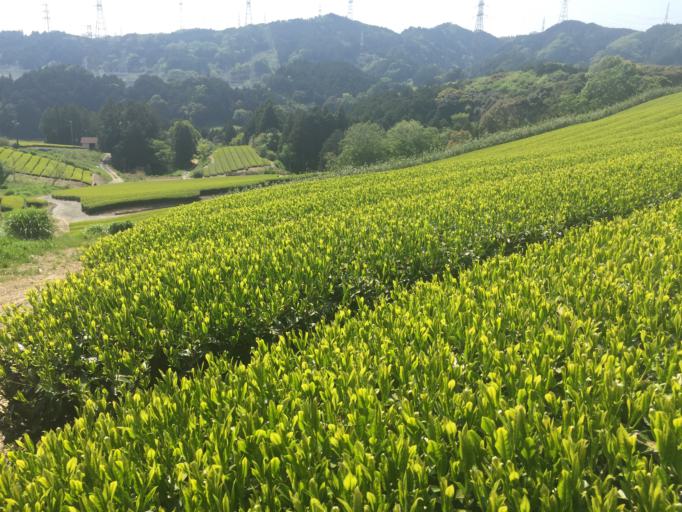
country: JP
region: Shizuoka
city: Kanaya
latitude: 34.8128
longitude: 138.0724
